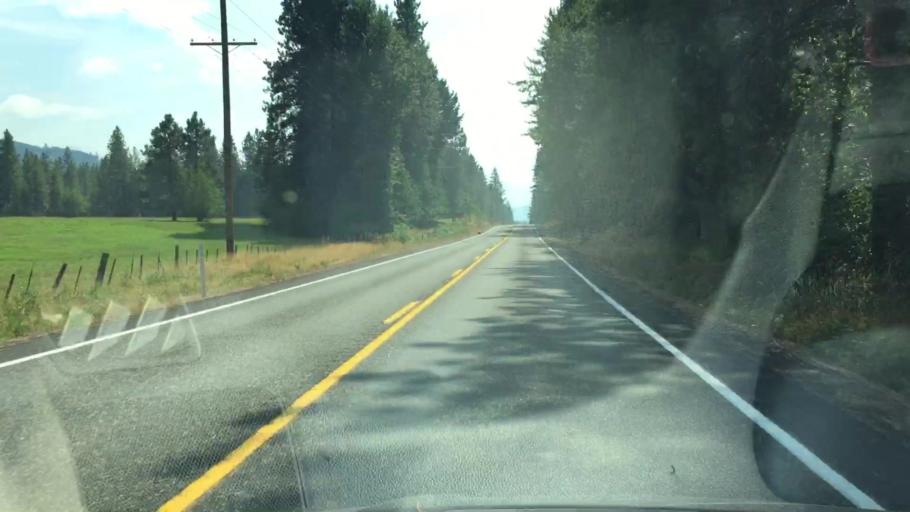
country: US
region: Washington
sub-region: Klickitat County
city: White Salmon
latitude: 45.9410
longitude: -121.4920
